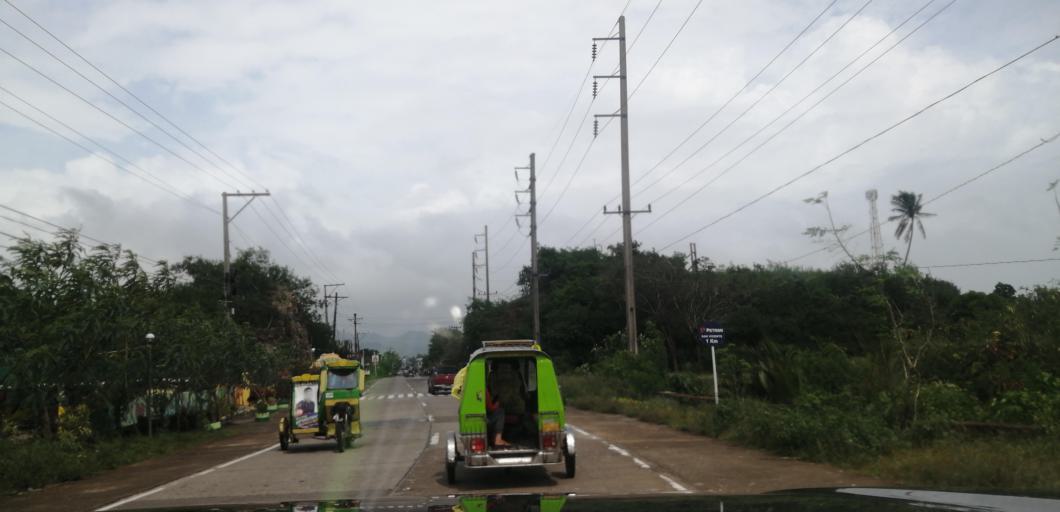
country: PH
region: Cagayan Valley
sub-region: Province of Cagayan
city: San Vicente
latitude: 18.4957
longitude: 122.1533
